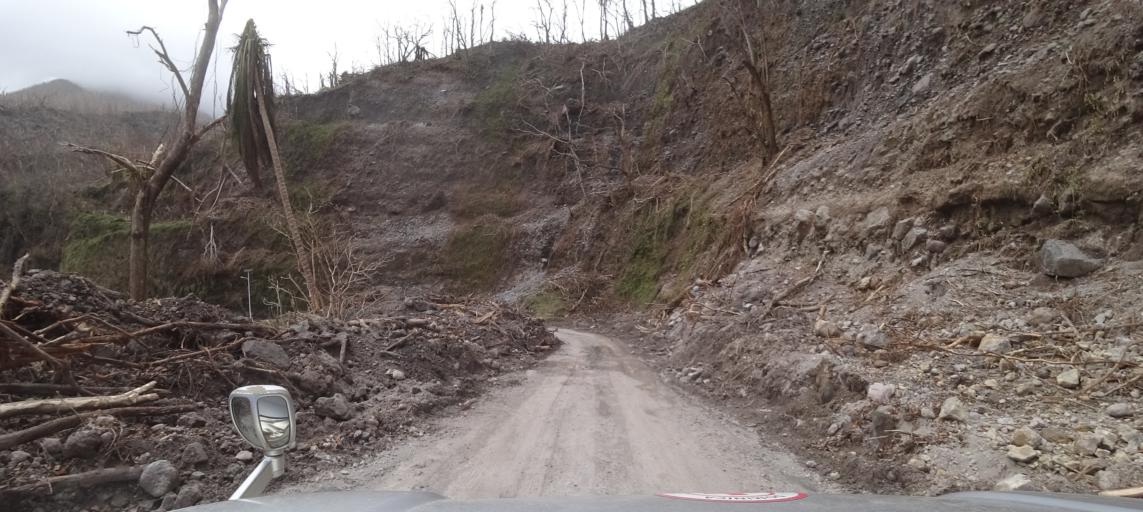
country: DM
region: Saint Patrick
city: La Plaine
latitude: 15.3123
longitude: -61.2498
